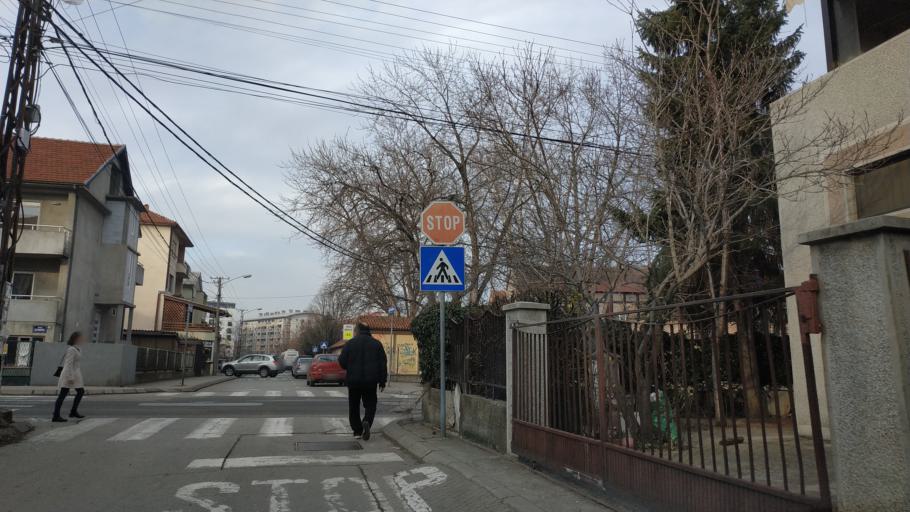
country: RS
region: Central Serbia
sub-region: Nisavski Okrug
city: Nis
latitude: 43.3189
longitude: 21.9306
